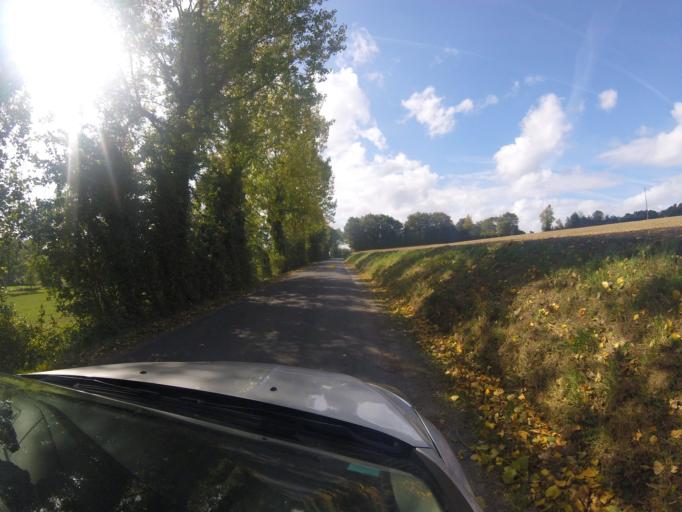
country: FR
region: Lower Normandy
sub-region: Departement du Calvados
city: Saint-Vigor-le-Grand
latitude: 49.3194
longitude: -0.6340
